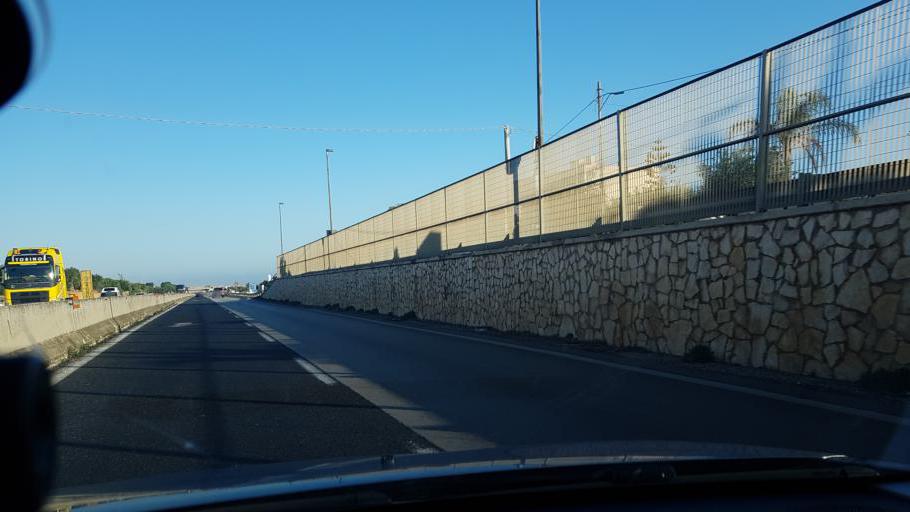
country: IT
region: Apulia
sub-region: Provincia di Brindisi
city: Fasano
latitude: 40.8840
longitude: 17.3364
